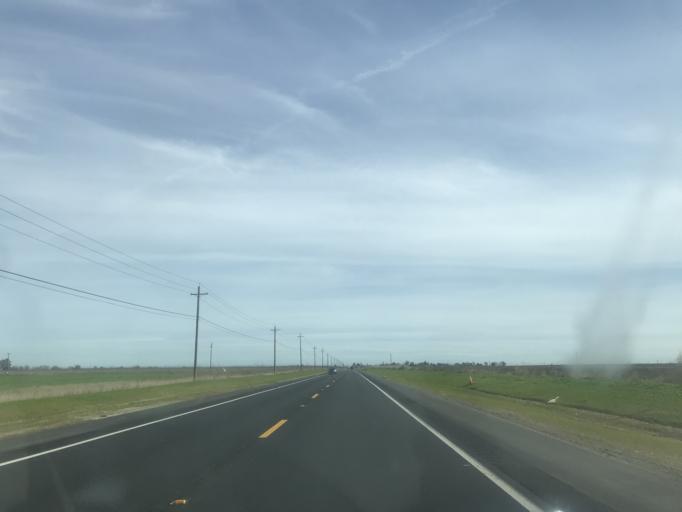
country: US
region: California
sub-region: Yolo County
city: Esparto
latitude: 38.6854
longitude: -121.9937
